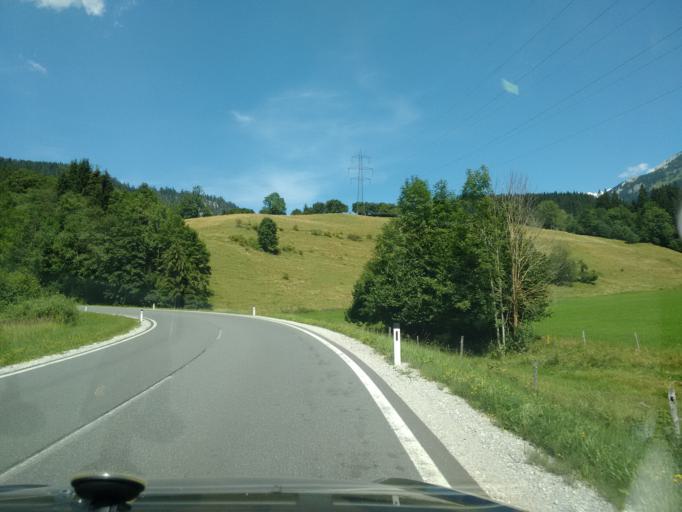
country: AT
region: Styria
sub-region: Politischer Bezirk Liezen
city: Ardning
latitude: 47.6065
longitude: 14.2896
